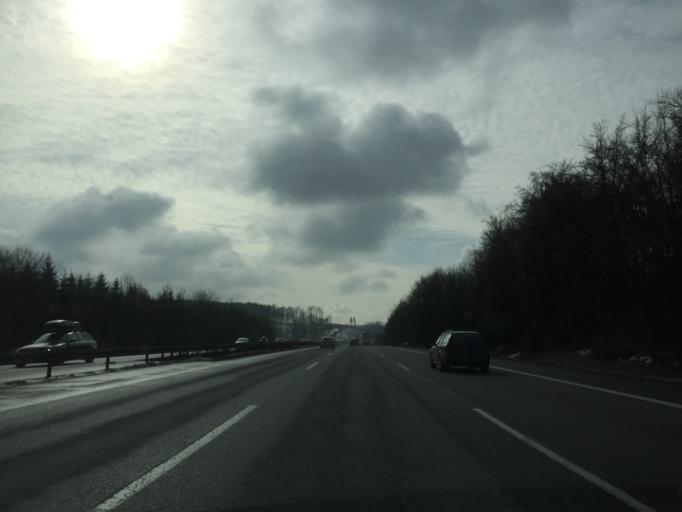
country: DE
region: Bavaria
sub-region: Upper Bavaria
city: Denkendorf
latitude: 48.9086
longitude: 11.4701
